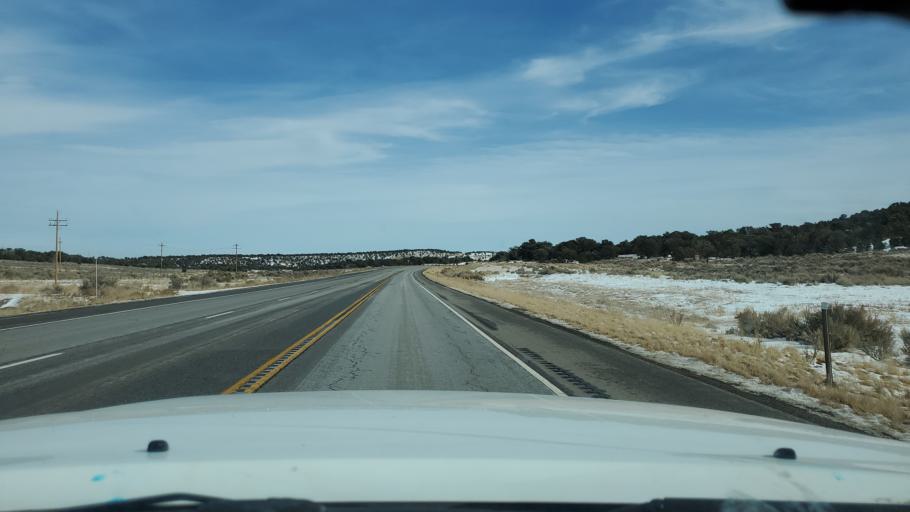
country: US
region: Utah
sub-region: Duchesne County
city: Duchesne
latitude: 40.1795
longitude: -110.6092
